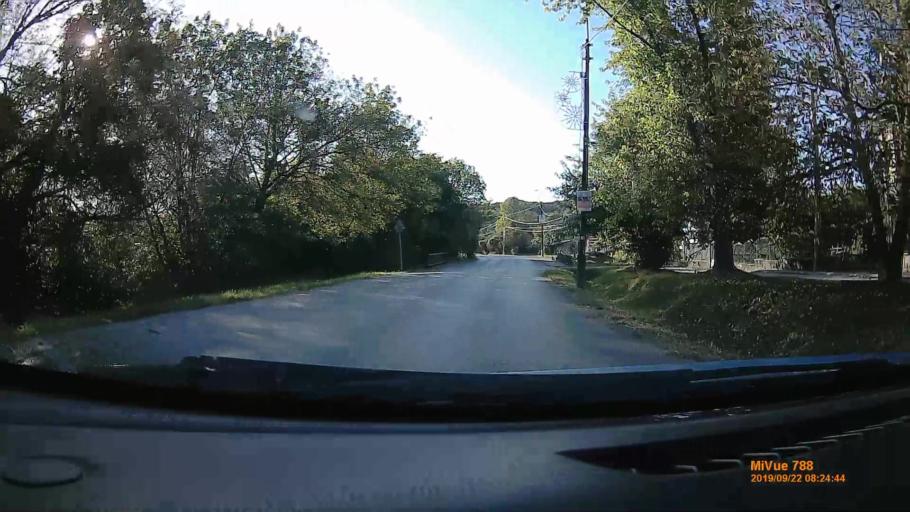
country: HU
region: Borsod-Abauj-Zemplen
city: Miskolc
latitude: 48.0895
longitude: 20.7129
